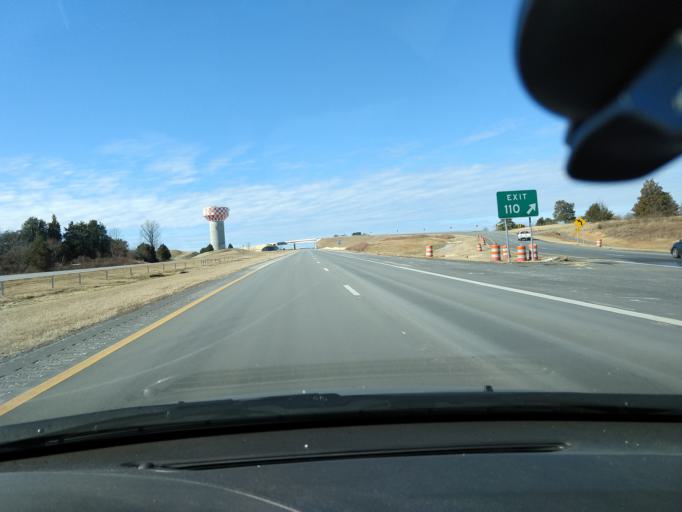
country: US
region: North Carolina
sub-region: Guilford County
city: Oak Ridge
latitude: 36.1212
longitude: -79.9541
